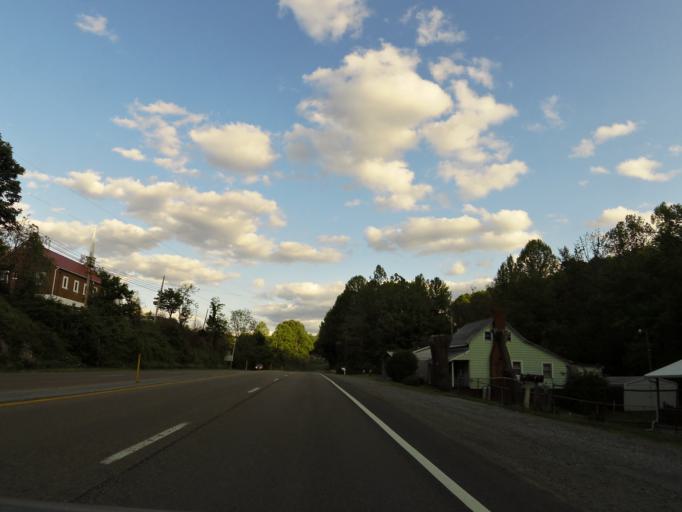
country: US
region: Virginia
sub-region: Washington County
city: Abingdon
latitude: 36.7379
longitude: -82.0391
